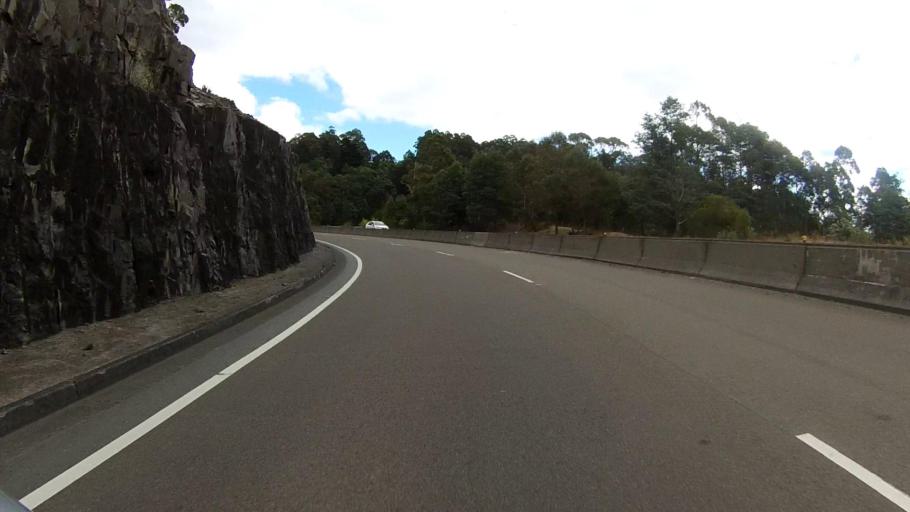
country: AU
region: Tasmania
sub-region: Kingborough
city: Margate
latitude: -42.9811
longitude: 147.1764
